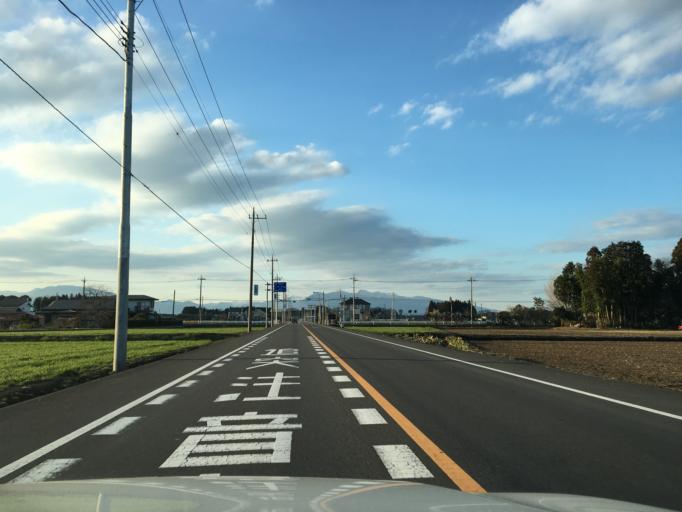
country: JP
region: Tochigi
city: Otawara
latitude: 36.8822
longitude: 140.0636
